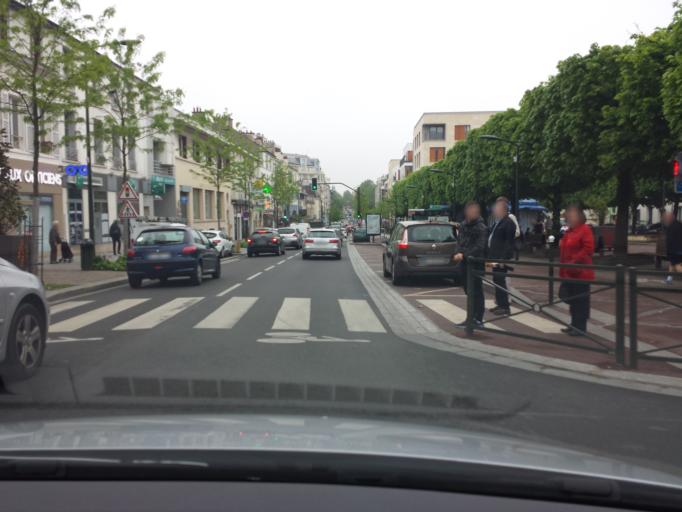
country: FR
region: Ile-de-France
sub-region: Departement des Hauts-de-Seine
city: Bourg-la-Reine
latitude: 48.7793
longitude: 2.3153
